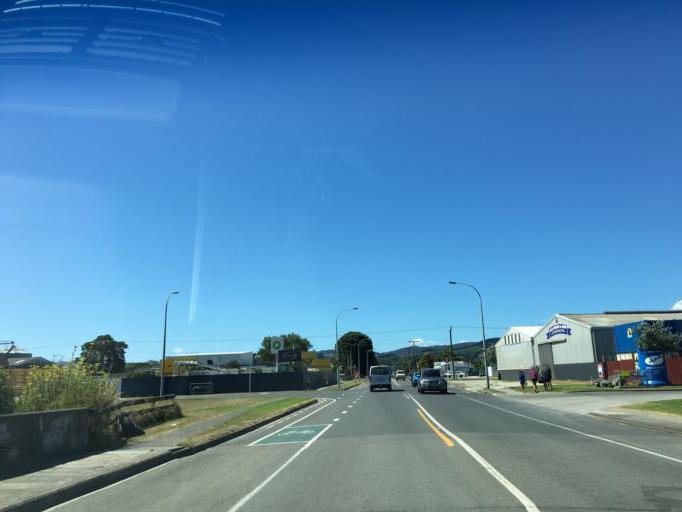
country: NZ
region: Gisborne
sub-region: Gisborne District
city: Gisborne
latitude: -38.6652
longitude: 178.0056
